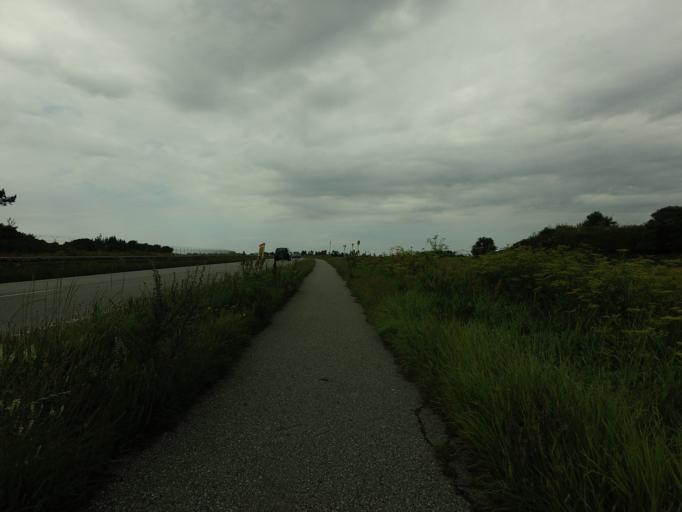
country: DK
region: North Denmark
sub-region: Alborg Kommune
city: Vadum
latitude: 57.1070
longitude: 9.8778
